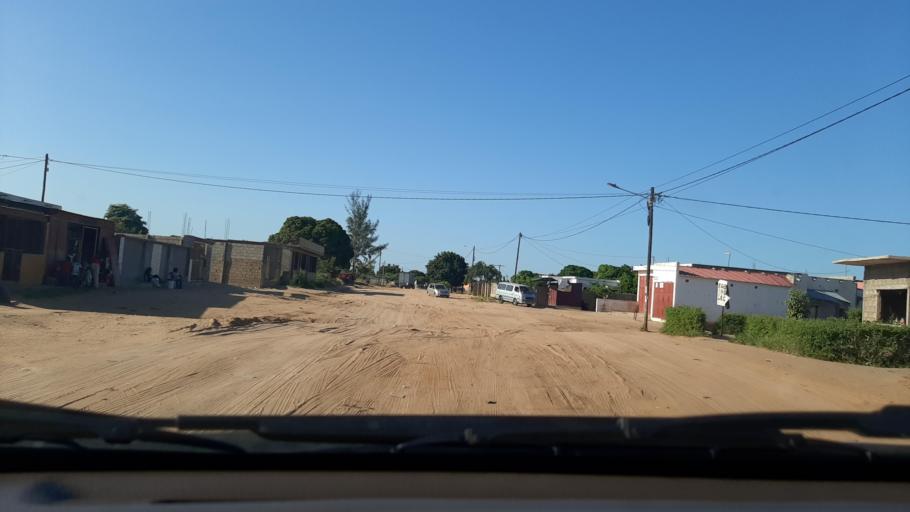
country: MZ
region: Maputo City
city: Maputo
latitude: -25.8050
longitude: 32.5469
